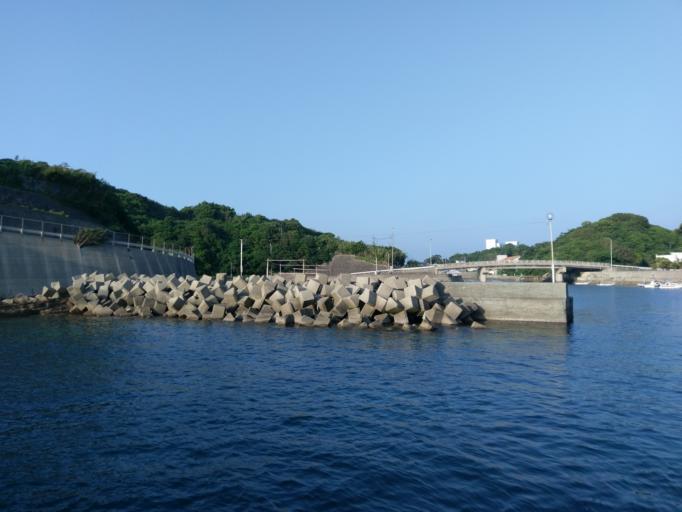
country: JP
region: Nagasaki
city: Nagasaki-shi
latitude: 32.7014
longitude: 129.7738
